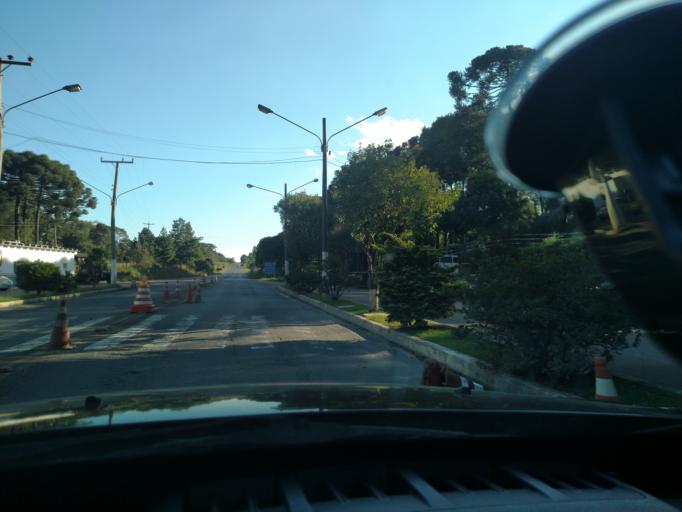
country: BR
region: Santa Catarina
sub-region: Otacilio Costa
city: Otacilio Costa
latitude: -27.5896
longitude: -50.1675
